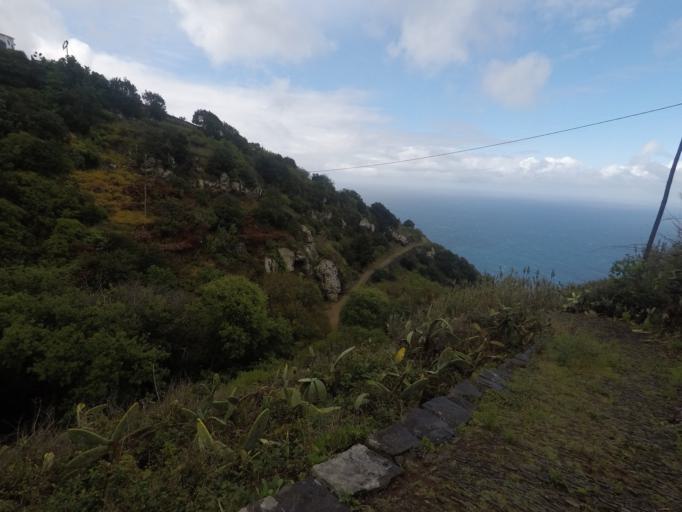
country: PT
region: Madeira
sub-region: Calheta
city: Faja da Ovelha
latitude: 32.7718
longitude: -17.2353
